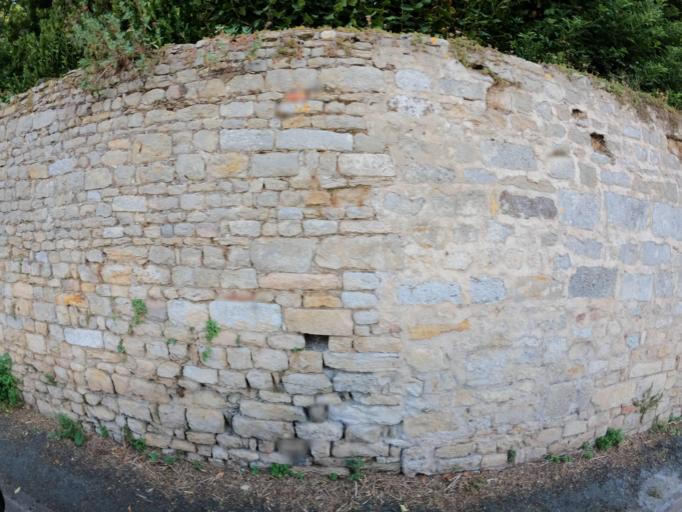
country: FR
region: Pays de la Loire
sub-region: Departement de la Vendee
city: Triaize
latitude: 46.3527
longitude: -1.2498
